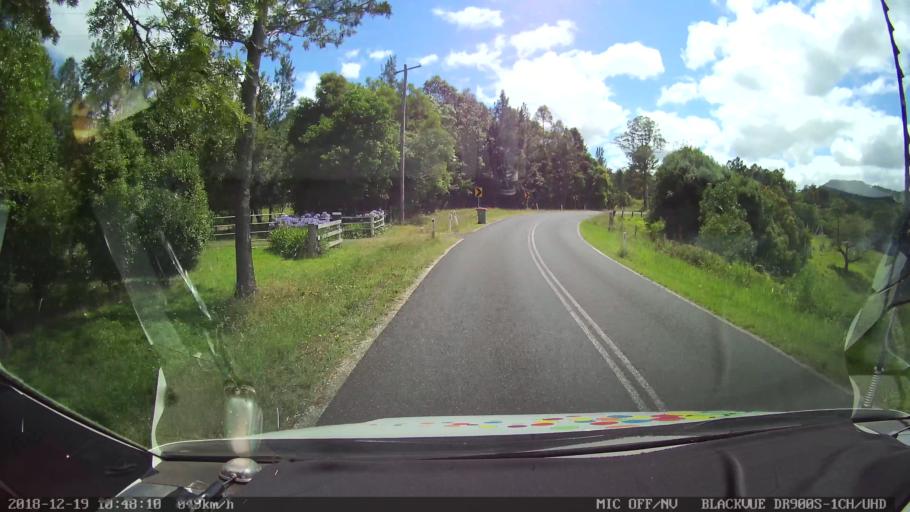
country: AU
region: New South Wales
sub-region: Lismore Municipality
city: Nimbin
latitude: -28.6044
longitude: 153.2108
